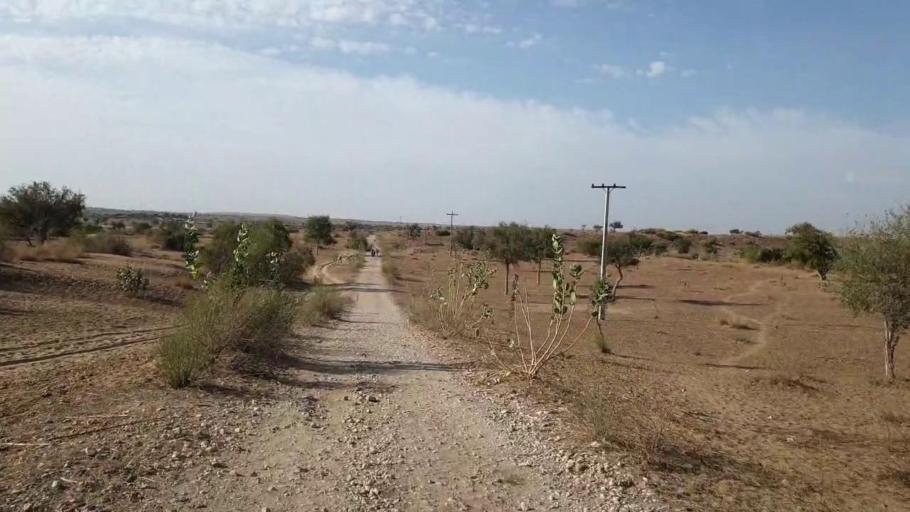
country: PK
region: Sindh
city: Nabisar
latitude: 25.0443
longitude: 69.9743
